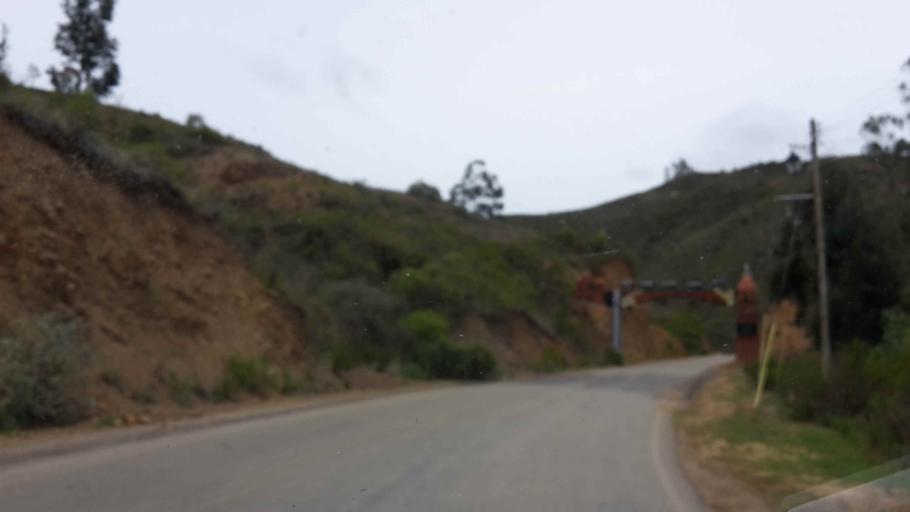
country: BO
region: Cochabamba
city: Totora
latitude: -17.7286
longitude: -65.1922
